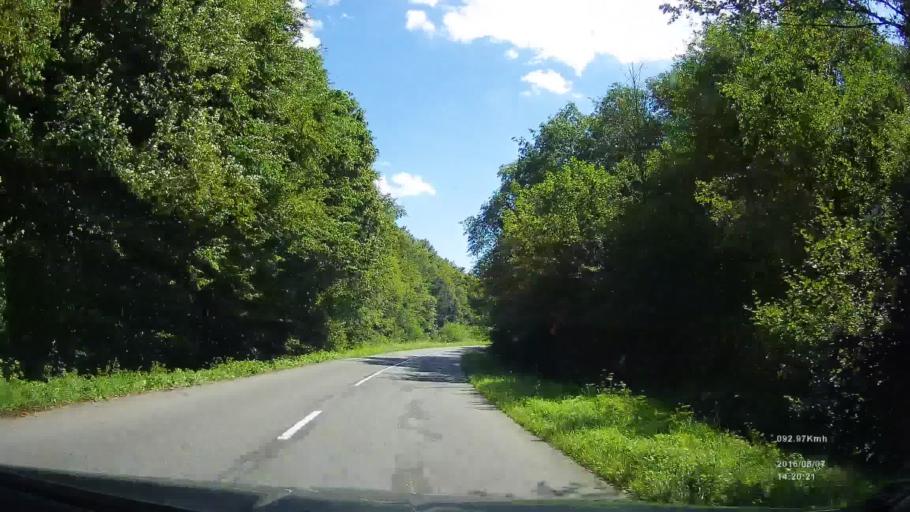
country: SK
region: Presovsky
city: Stropkov
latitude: 49.2915
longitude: 21.7611
